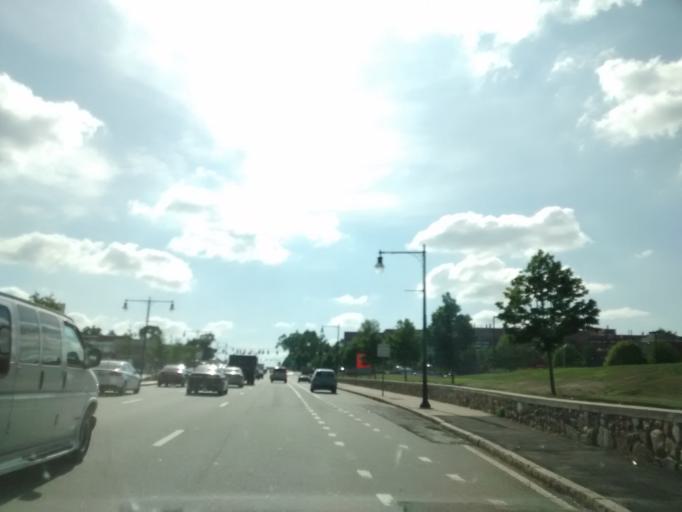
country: US
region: Massachusetts
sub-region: Worcester County
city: Hamilton
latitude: 42.2739
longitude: -71.7654
